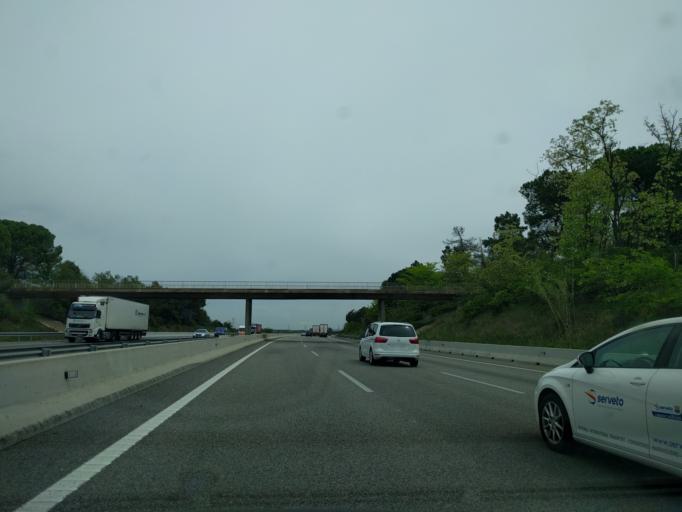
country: ES
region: Catalonia
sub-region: Provincia de Girona
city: Vilobi d'Onyar
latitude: 41.8660
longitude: 2.7561
